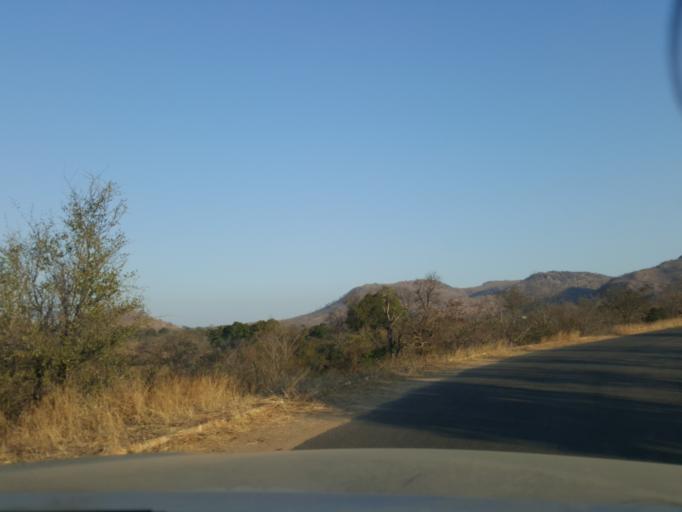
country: SZ
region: Hhohho
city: Ntfonjeni
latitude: -25.4374
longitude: 31.4451
